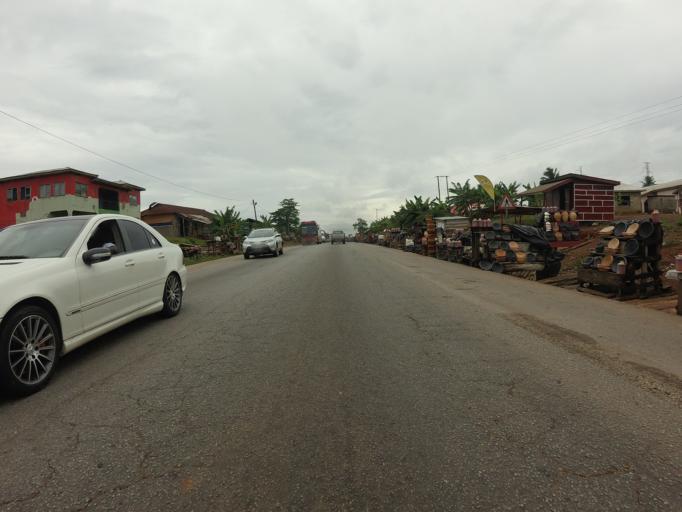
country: GH
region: Eastern
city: Nkawkaw
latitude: 6.4496
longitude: -0.6109
